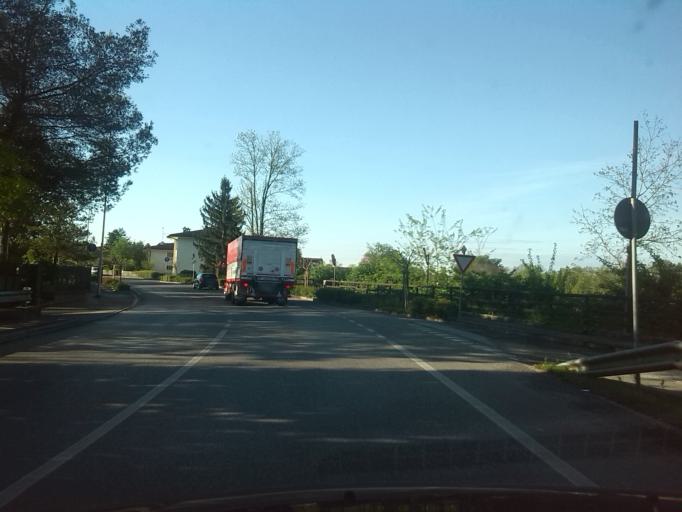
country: IT
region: Friuli Venezia Giulia
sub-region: Provincia di Udine
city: Corno di Rosazzo
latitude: 46.0040
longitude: 13.4377
